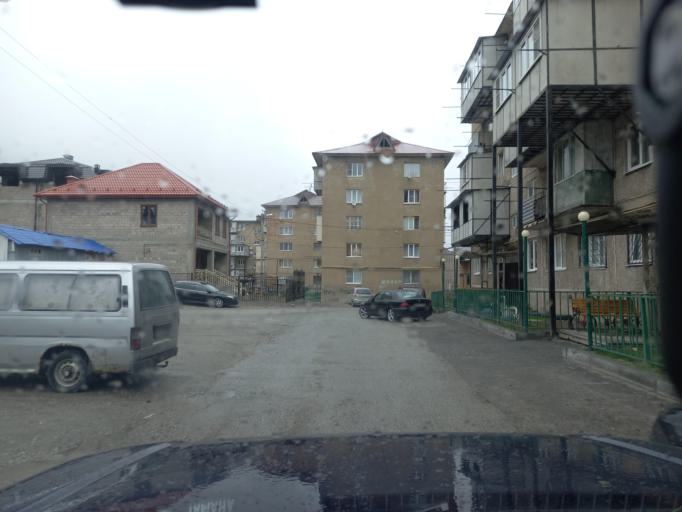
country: RU
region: Kabardino-Balkariya
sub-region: El'brusskiy Rayon
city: El'brus
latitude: 43.2573
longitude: 42.6451
